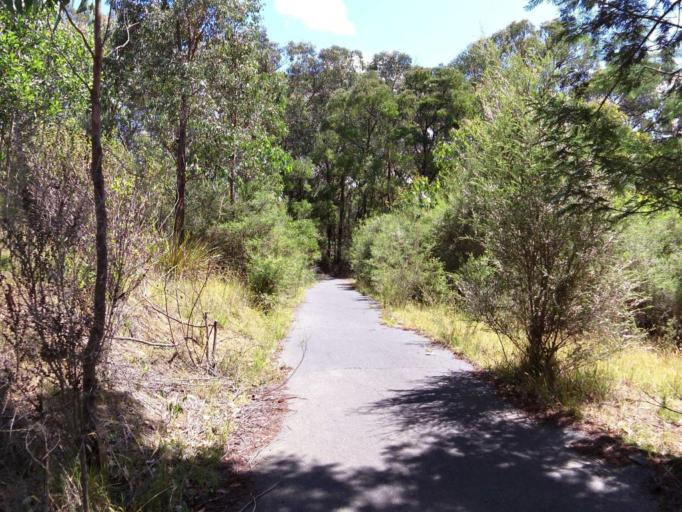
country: AU
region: Victoria
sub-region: Cardinia
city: Officer
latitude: -38.0311
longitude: 145.4284
